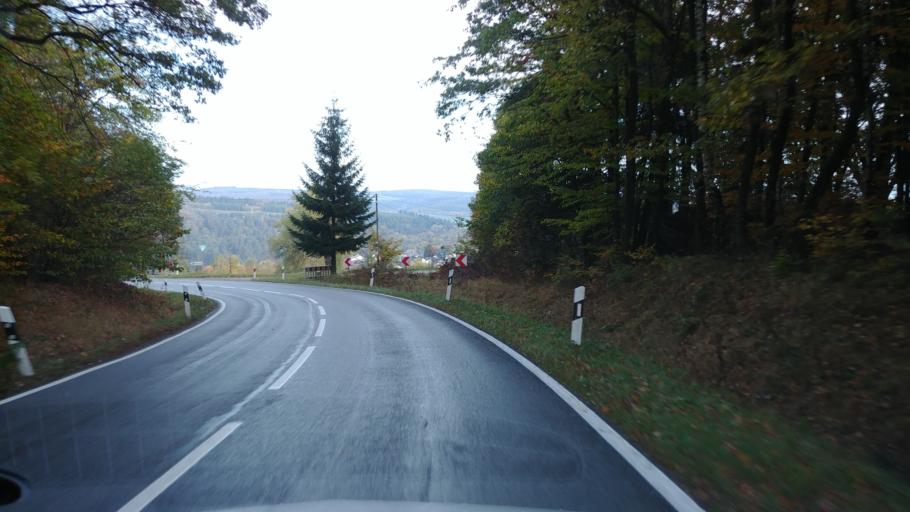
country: DE
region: Hesse
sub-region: Regierungsbezirk Darmstadt
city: Schlangenbad
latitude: 50.1201
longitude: 8.1213
